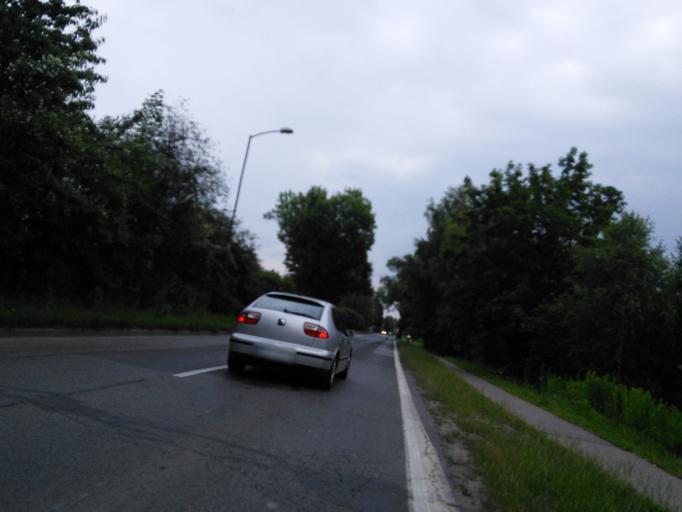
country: PL
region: Silesian Voivodeship
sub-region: Piekary Slaskie
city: Brzeziny Slaskie
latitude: 50.3703
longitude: 18.9668
